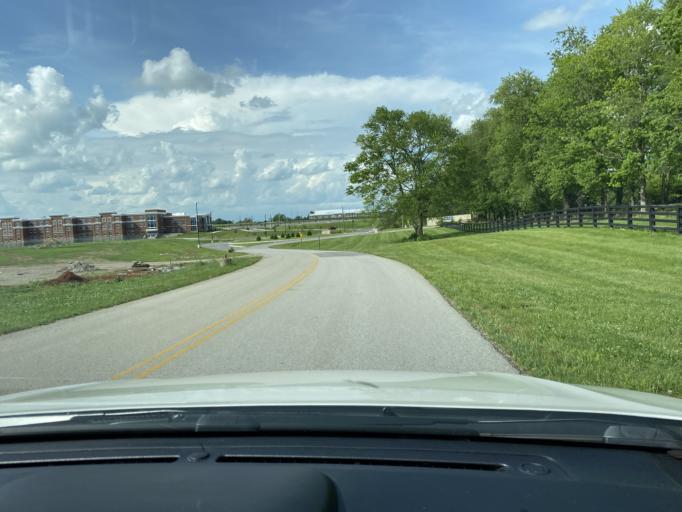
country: US
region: Kentucky
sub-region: Scott County
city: Georgetown
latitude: 38.2122
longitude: -84.5988
